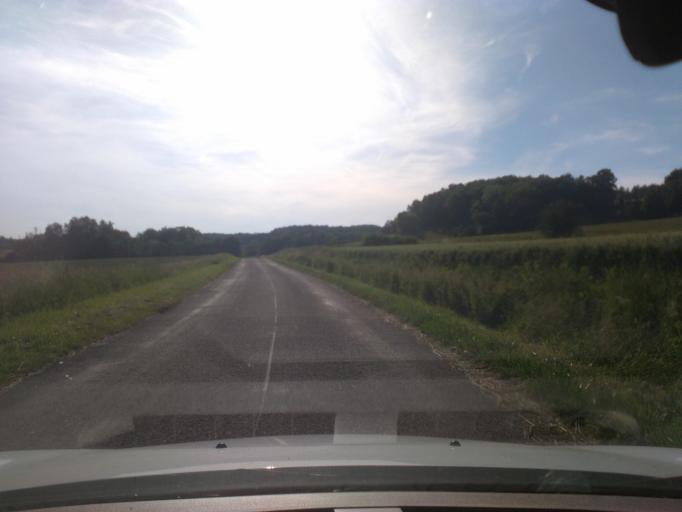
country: FR
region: Lorraine
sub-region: Departement des Vosges
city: Mirecourt
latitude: 48.2672
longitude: 6.2149
